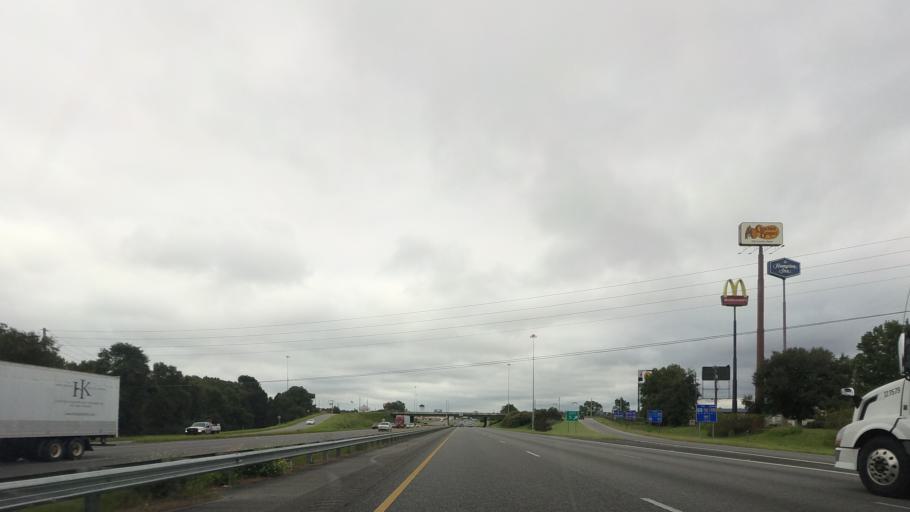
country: US
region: Georgia
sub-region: Lowndes County
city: Valdosta
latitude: 30.6817
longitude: -83.2249
